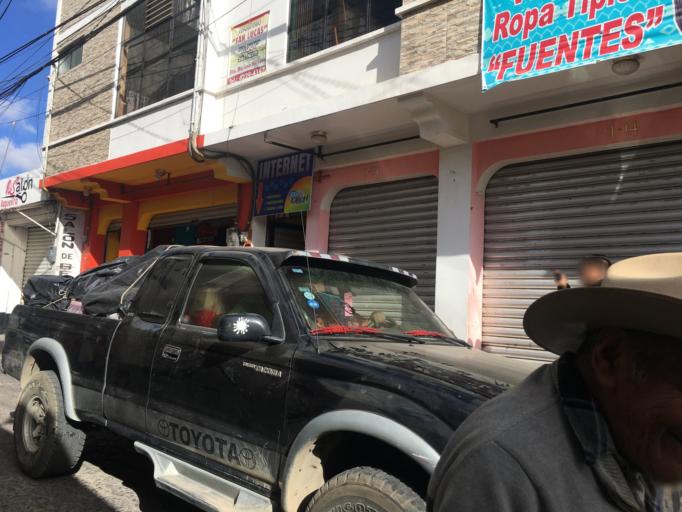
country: GT
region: Quetzaltenango
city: Ostuncalco
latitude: 14.8681
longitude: -91.6220
